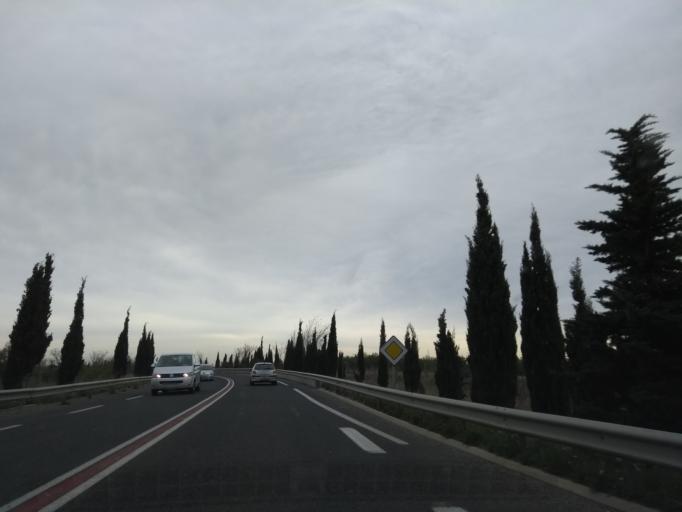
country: FR
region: Languedoc-Roussillon
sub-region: Departement des Pyrenees-Orientales
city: Toulouges
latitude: 42.6773
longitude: 2.8570
